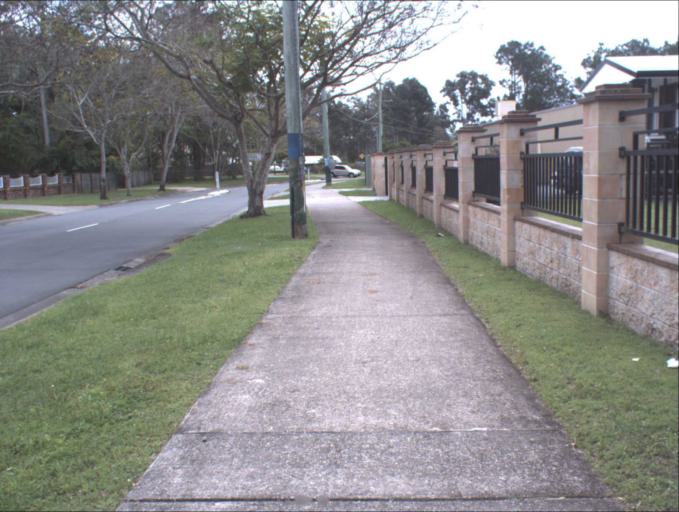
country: AU
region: Queensland
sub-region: Logan
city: Waterford West
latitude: -27.6970
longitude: 153.1301
